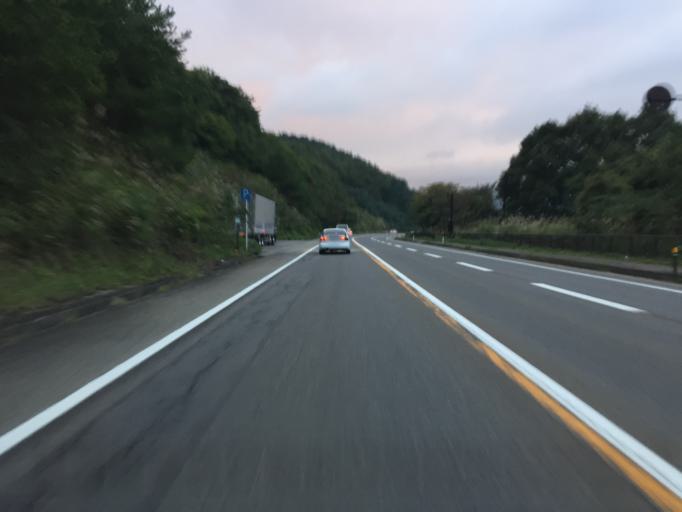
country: JP
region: Fukushima
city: Inawashiro
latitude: 37.5254
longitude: 139.9812
